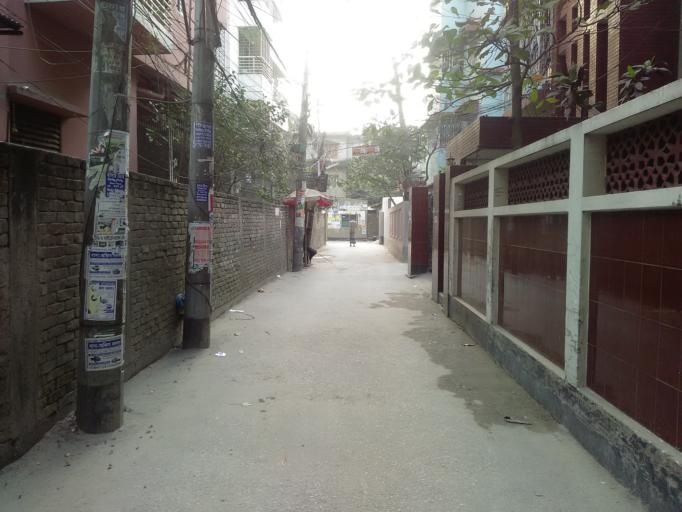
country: BD
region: Dhaka
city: Azimpur
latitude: 23.7768
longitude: 90.3669
